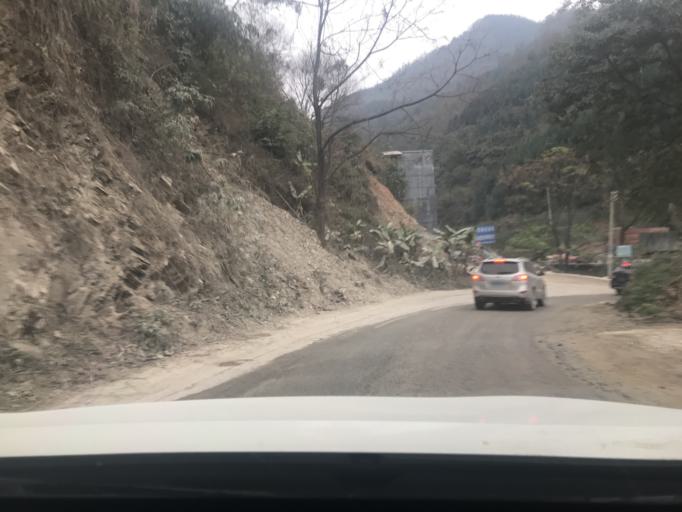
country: CN
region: Guangxi Zhuangzu Zizhiqu
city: Xinzhou
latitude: 24.9851
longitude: 105.8218
